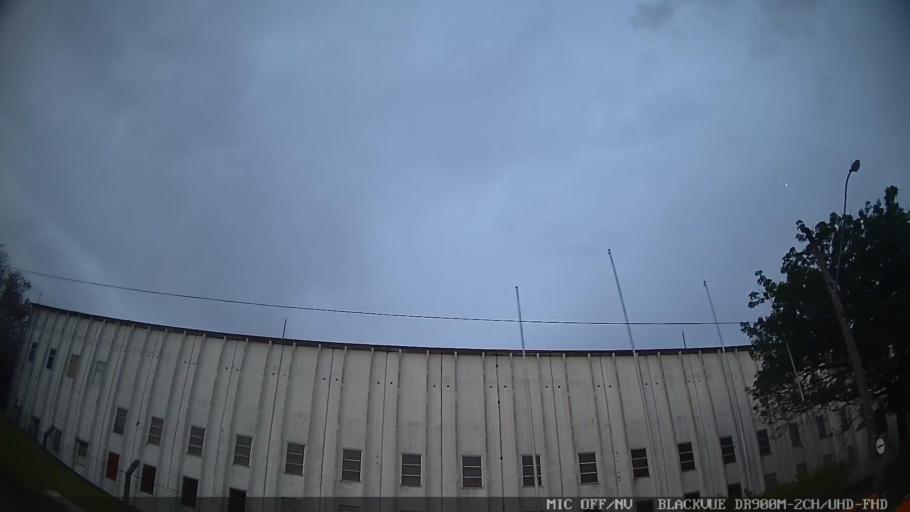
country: BR
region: Sao Paulo
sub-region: Vinhedo
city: Vinhedo
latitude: -23.0362
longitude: -46.9831
